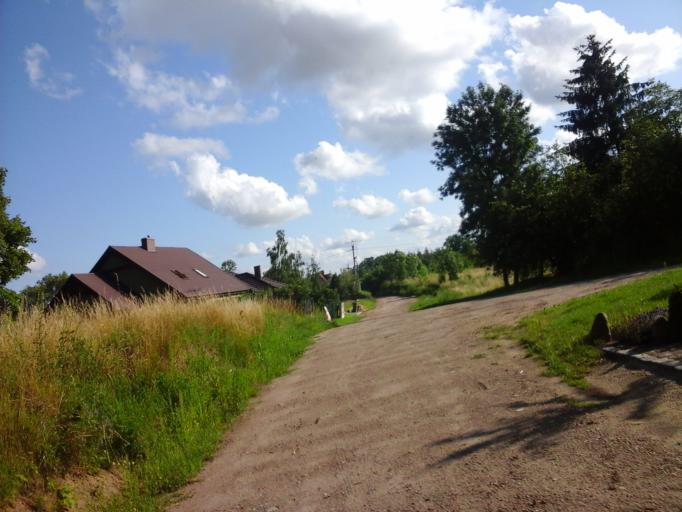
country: PL
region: West Pomeranian Voivodeship
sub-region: Powiat choszczenski
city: Choszczno
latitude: 53.1799
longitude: 15.4199
